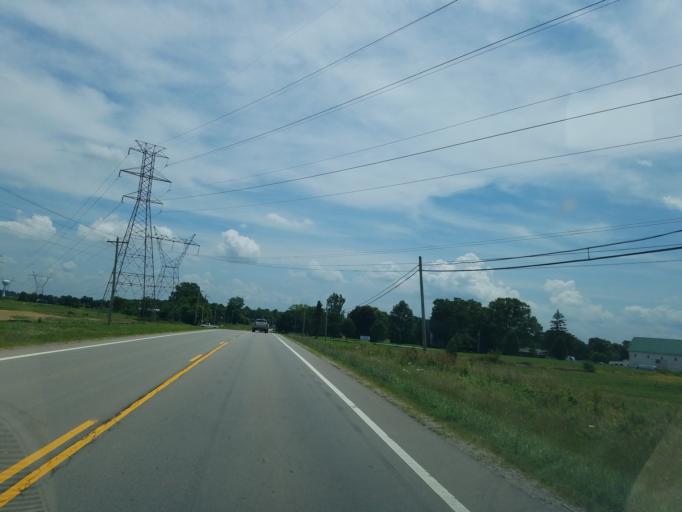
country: US
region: Ohio
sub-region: Delaware County
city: Sunbury
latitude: 40.2599
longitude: -82.8866
